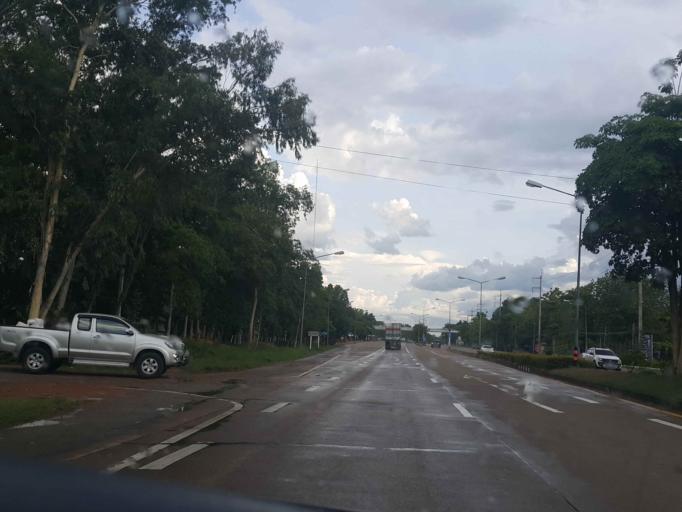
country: TH
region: Phrae
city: Den Chai
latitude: 17.9845
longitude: 100.0941
